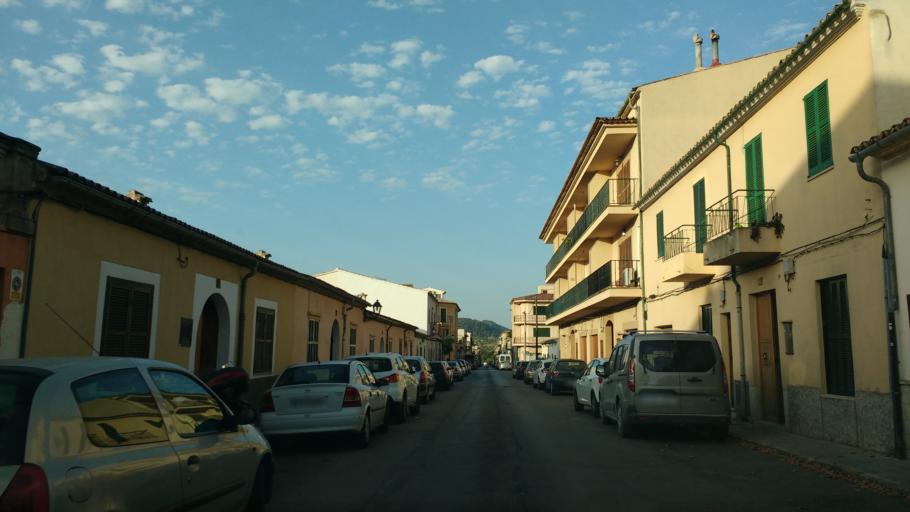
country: ES
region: Balearic Islands
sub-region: Illes Balears
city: Alaro
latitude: 39.7038
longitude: 2.7931
